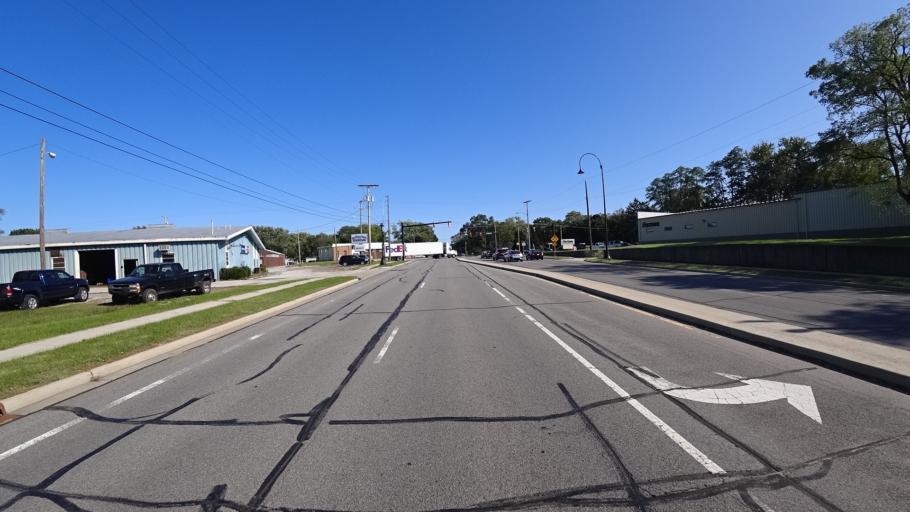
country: US
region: Indiana
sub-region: LaPorte County
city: Trail Creek
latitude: 41.7078
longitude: -86.8657
